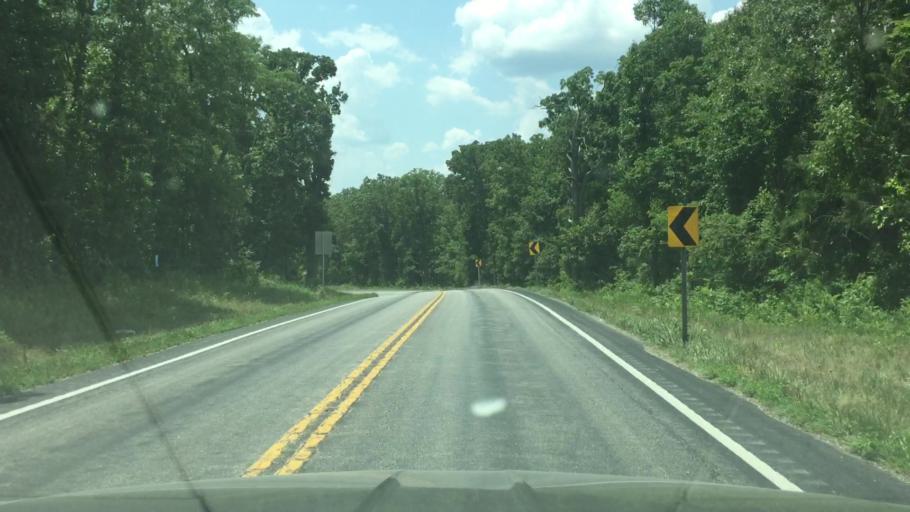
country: US
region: Missouri
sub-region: Camden County
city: Osage Beach
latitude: 38.1282
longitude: -92.5574
